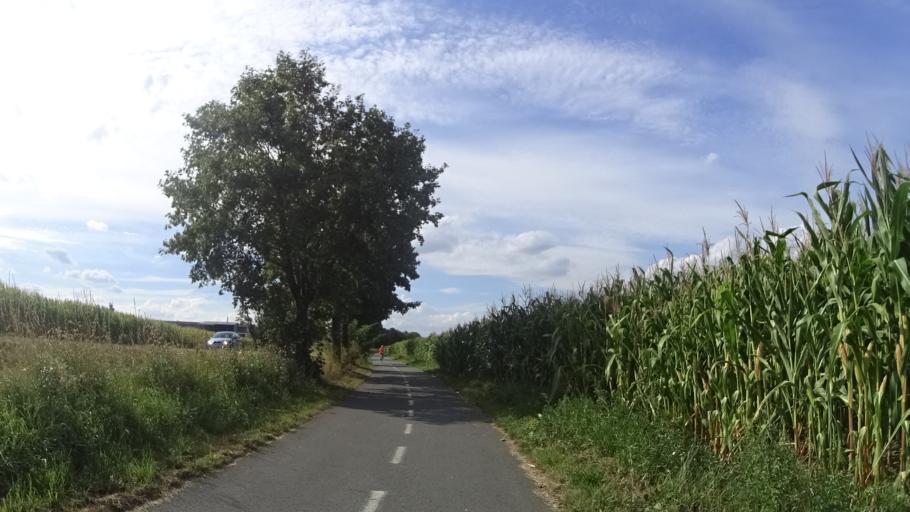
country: CZ
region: Olomoucky
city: Moravicany
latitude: 49.7697
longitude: 16.9453
